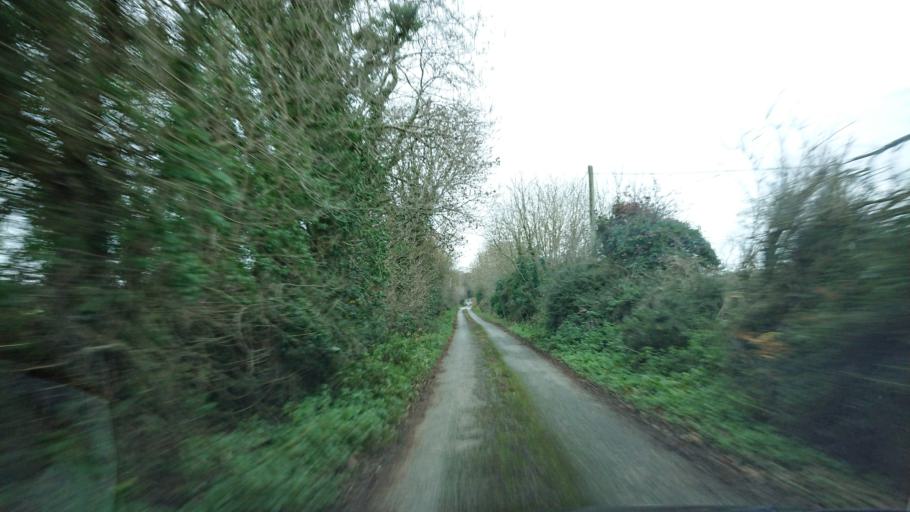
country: IE
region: Munster
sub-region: Waterford
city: Dunmore East
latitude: 52.1918
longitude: -7.0382
